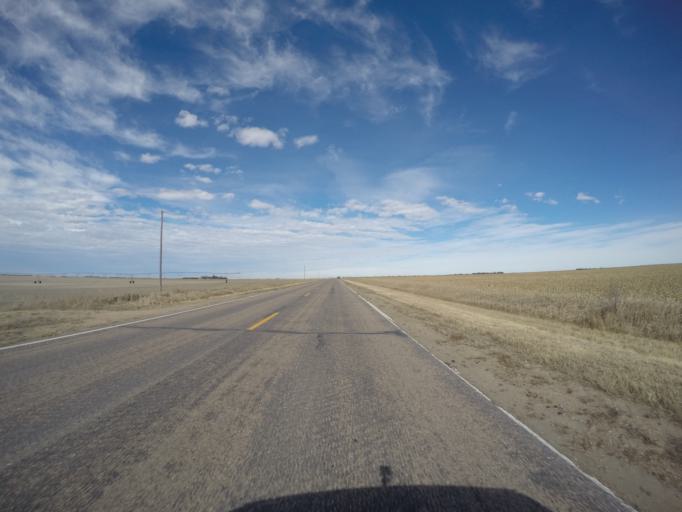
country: US
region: Nebraska
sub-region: Franklin County
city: Franklin
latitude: 40.2378
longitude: -98.9524
